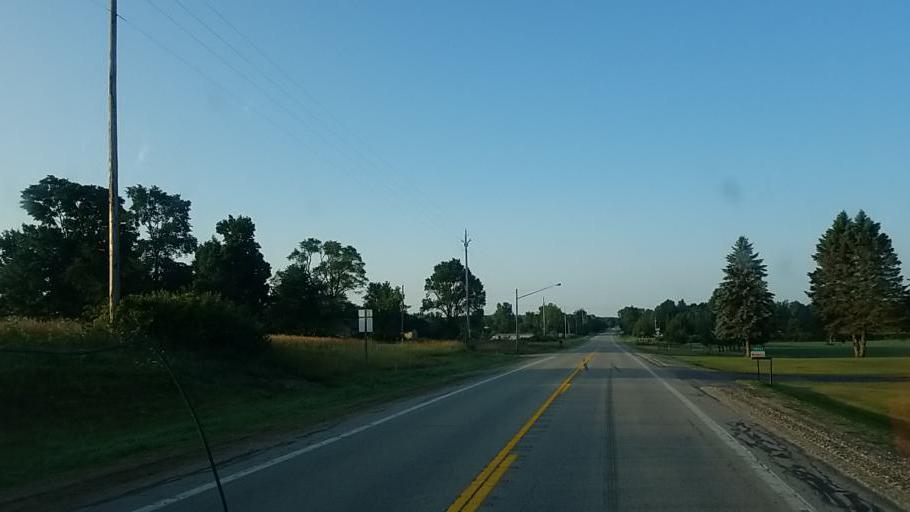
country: US
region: Michigan
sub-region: Isabella County
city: Lake Isabella
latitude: 43.6152
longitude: -85.1457
